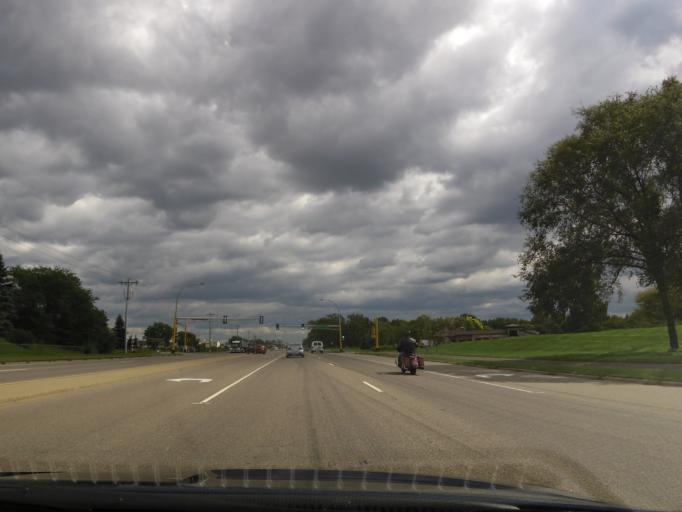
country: US
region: Minnesota
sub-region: Dakota County
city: Apple Valley
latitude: 44.7173
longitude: -93.2089
